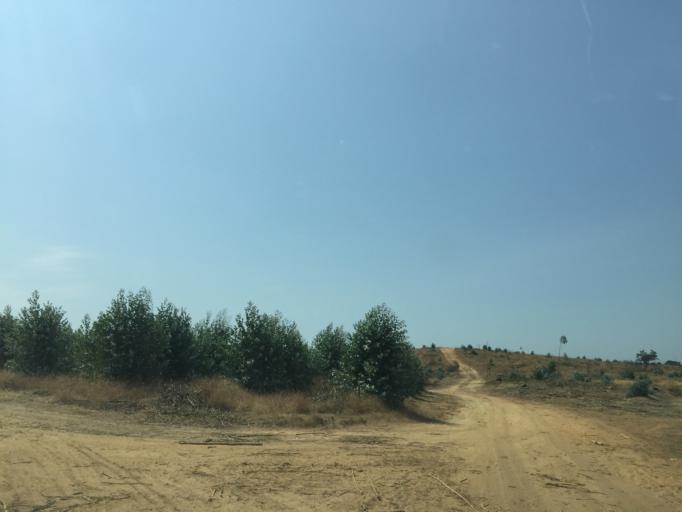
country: PT
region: Setubal
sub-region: Grandola
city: Grandola
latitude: 38.0476
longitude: -8.4670
